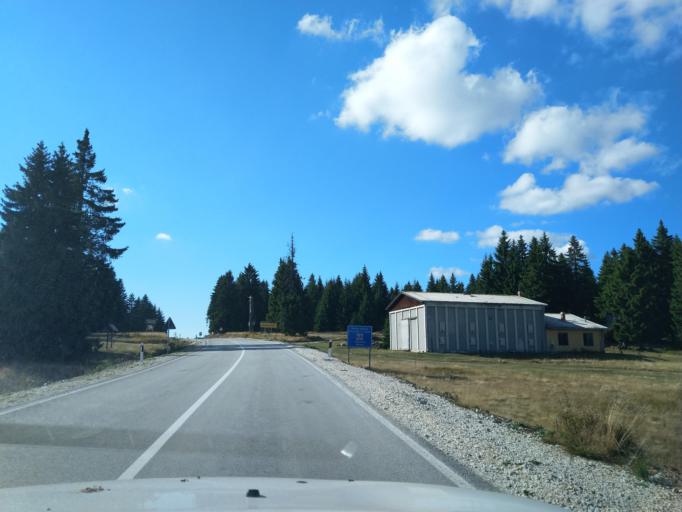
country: RS
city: Sokolovica
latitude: 43.2807
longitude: 20.3349
